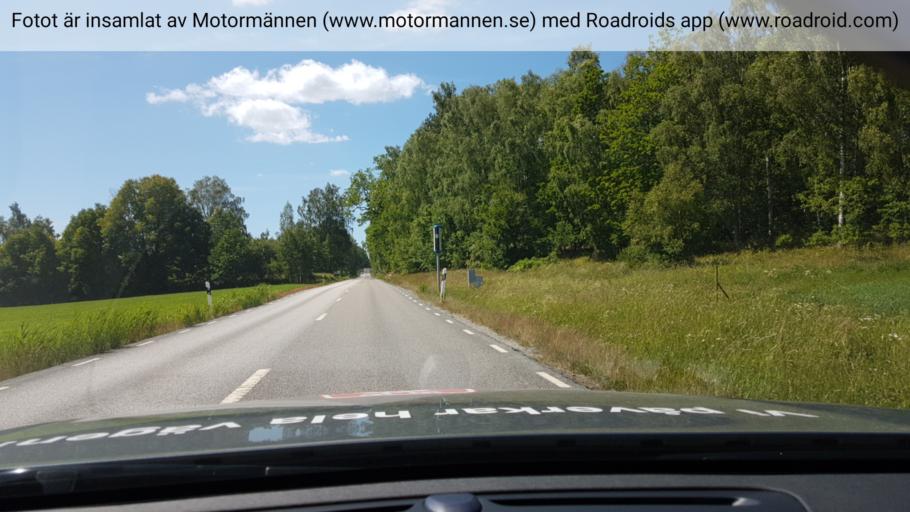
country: SE
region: Stockholm
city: Dalaro
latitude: 59.1327
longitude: 18.3525
